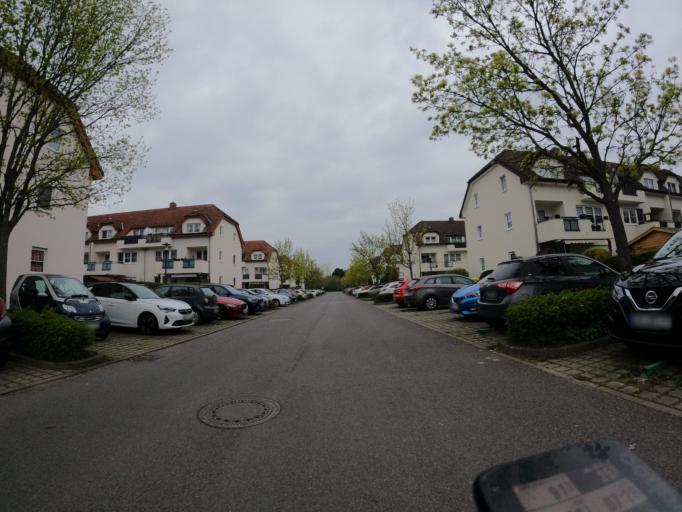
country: DE
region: Berlin
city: Gropiusstadt
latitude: 52.4120
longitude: 13.4489
